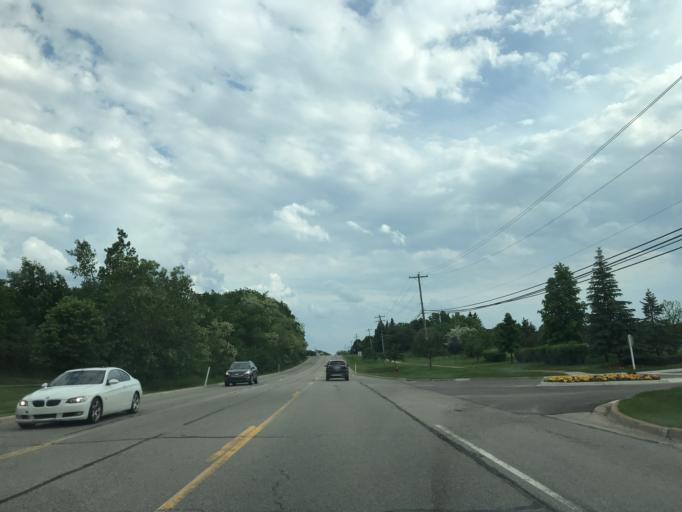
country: US
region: Michigan
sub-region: Oakland County
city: Novi
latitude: 42.4735
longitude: -83.4555
